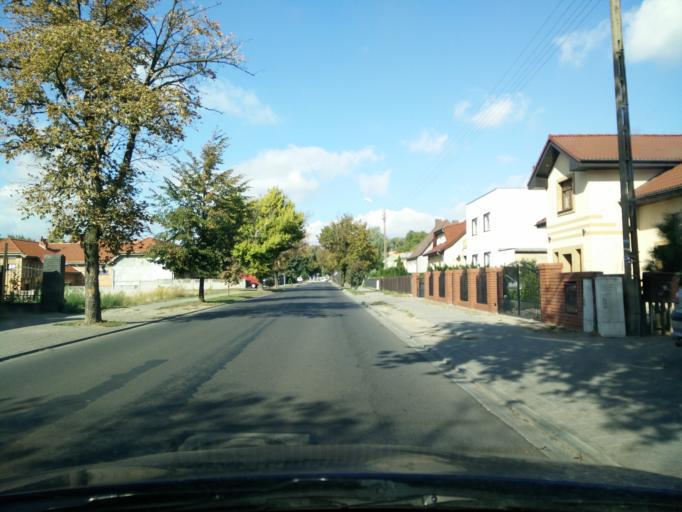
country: PL
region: Greater Poland Voivodeship
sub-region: Powiat sredzki
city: Sroda Wielkopolska
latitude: 52.2309
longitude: 17.2865
